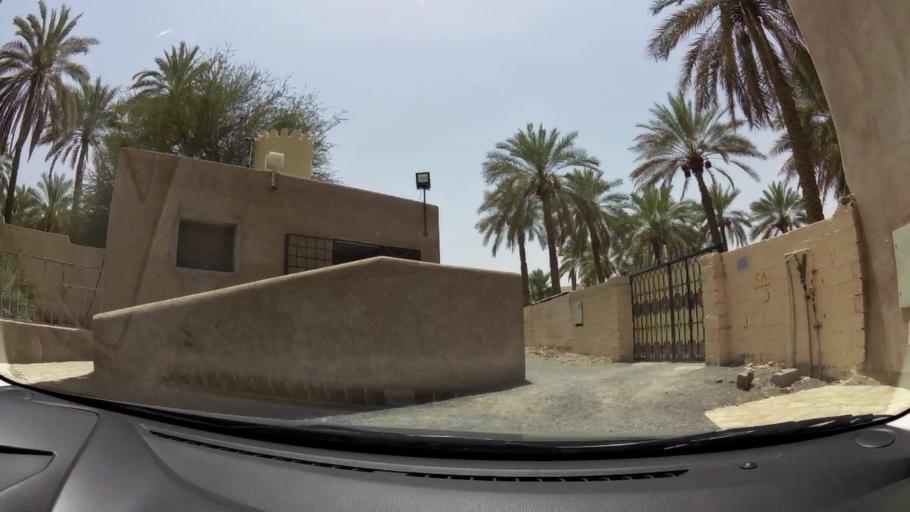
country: OM
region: Muhafazat Masqat
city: Bawshar
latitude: 23.5342
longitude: 58.3911
